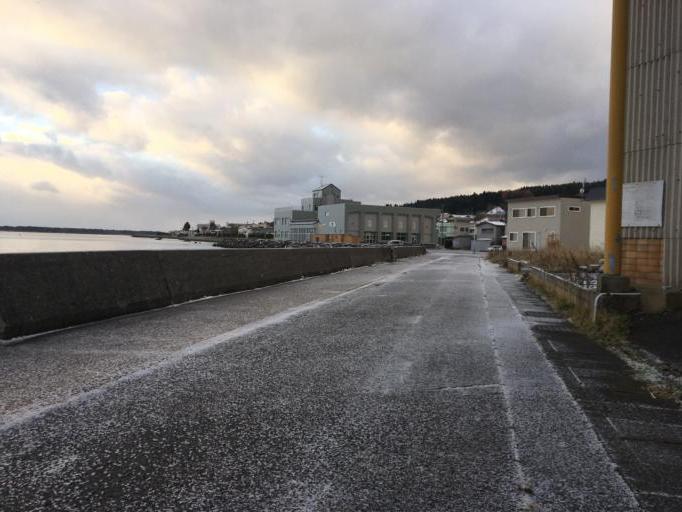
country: JP
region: Aomori
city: Mutsu
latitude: 41.2767
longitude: 141.1580
